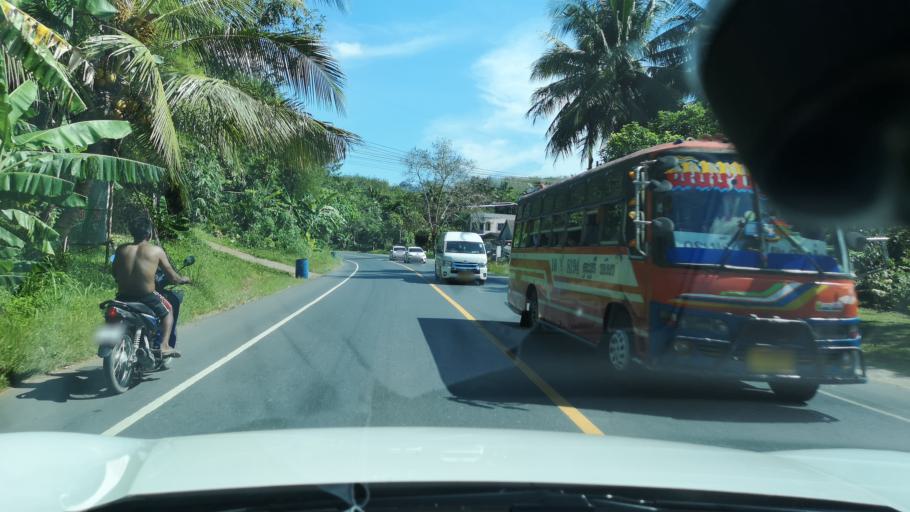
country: TH
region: Phangnga
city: Phang Nga
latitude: 8.5346
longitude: 98.5020
